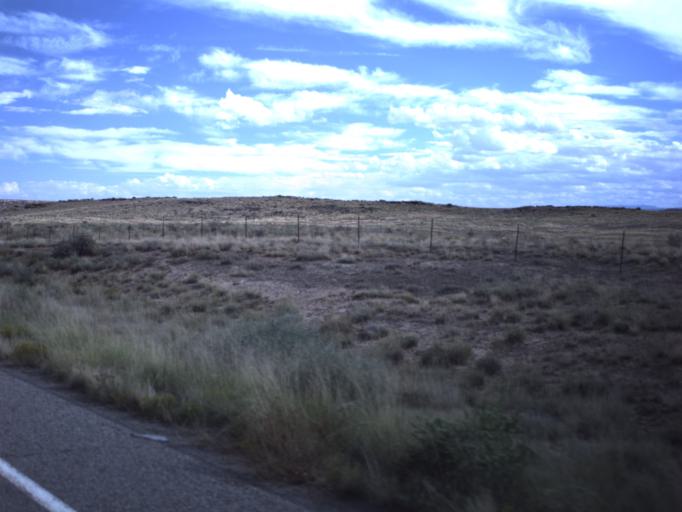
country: US
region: Colorado
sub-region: Montezuma County
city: Towaoc
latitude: 37.1673
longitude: -109.0814
